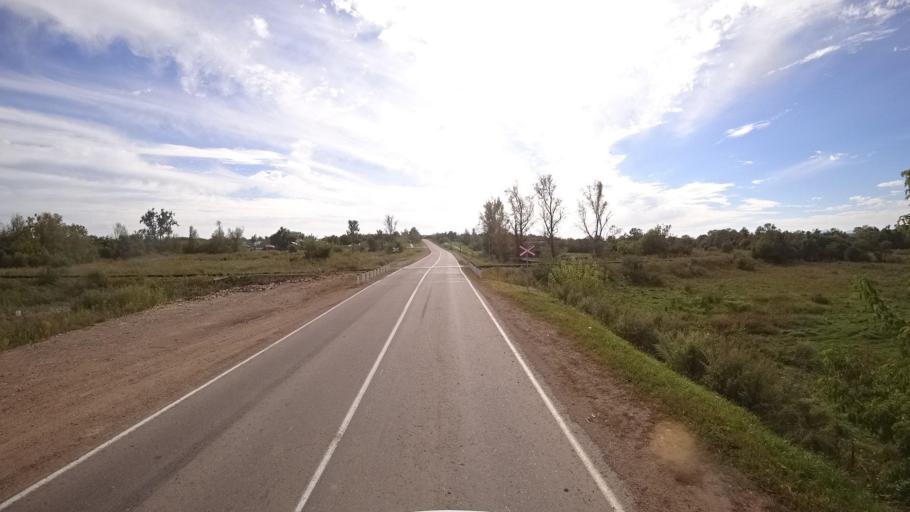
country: RU
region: Primorskiy
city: Dostoyevka
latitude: 44.3106
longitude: 133.4559
